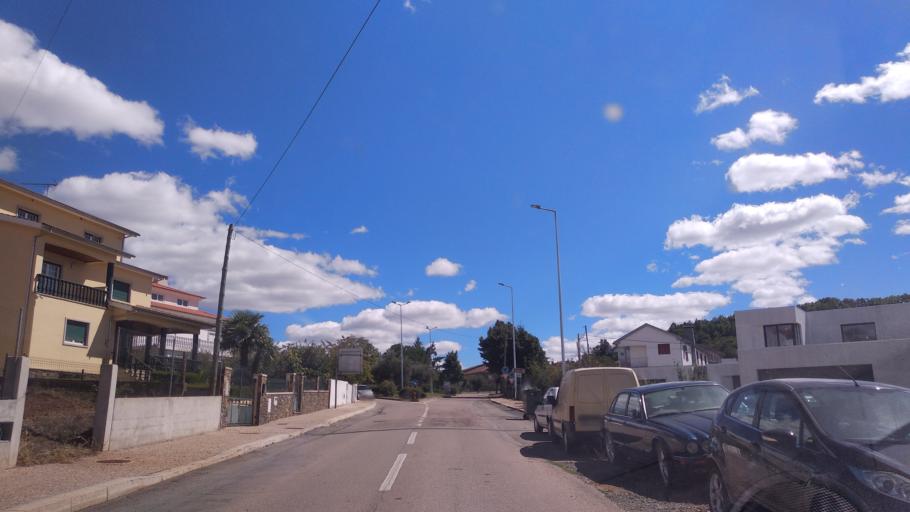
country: PT
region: Braganca
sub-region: Braganca Municipality
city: Braganca
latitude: 41.7848
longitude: -6.7662
